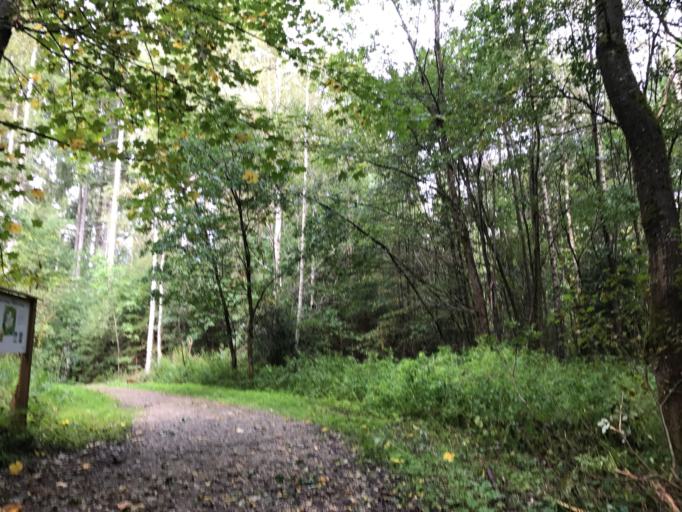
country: DE
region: Bavaria
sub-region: Upper Bavaria
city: Grunwald
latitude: 48.0230
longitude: 11.5256
